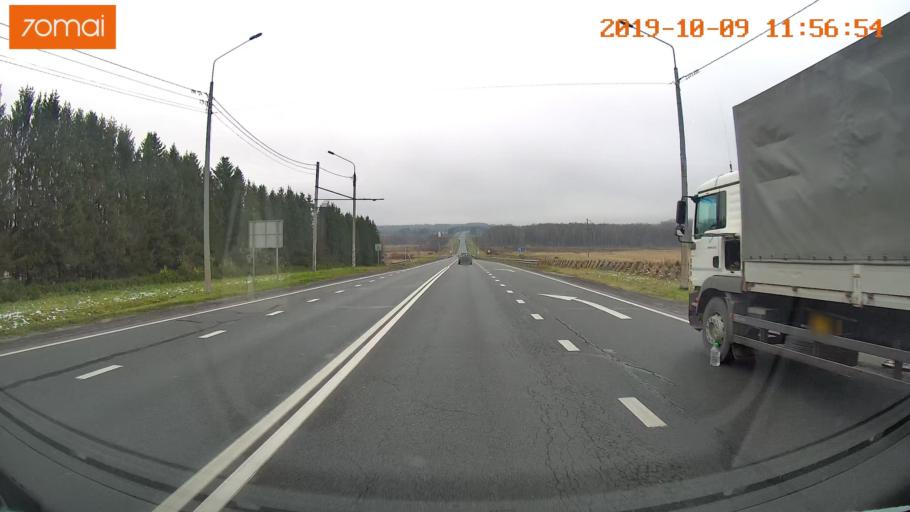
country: RU
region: Vologda
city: Gryazovets
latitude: 58.7388
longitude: 40.2898
